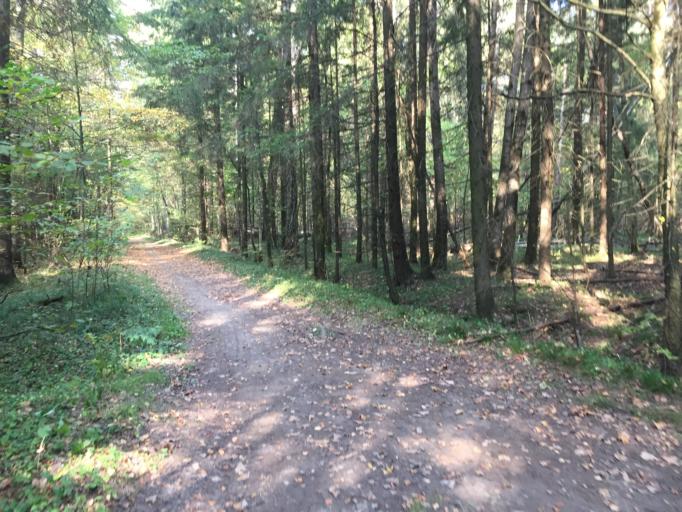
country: RU
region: Moscow
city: Babushkin
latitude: 55.8592
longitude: 37.7434
